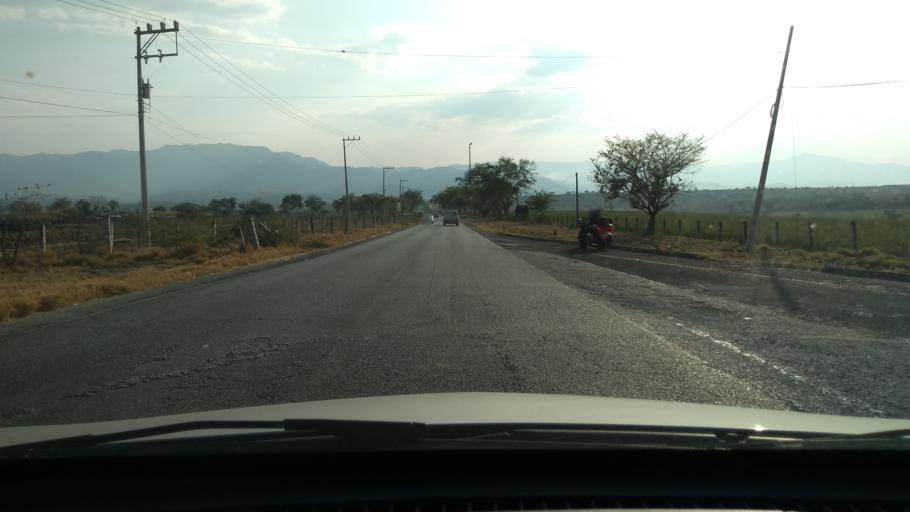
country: MX
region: Morelos
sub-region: Jojutla
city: Tehuixtla
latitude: 18.5874
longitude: -99.2609
